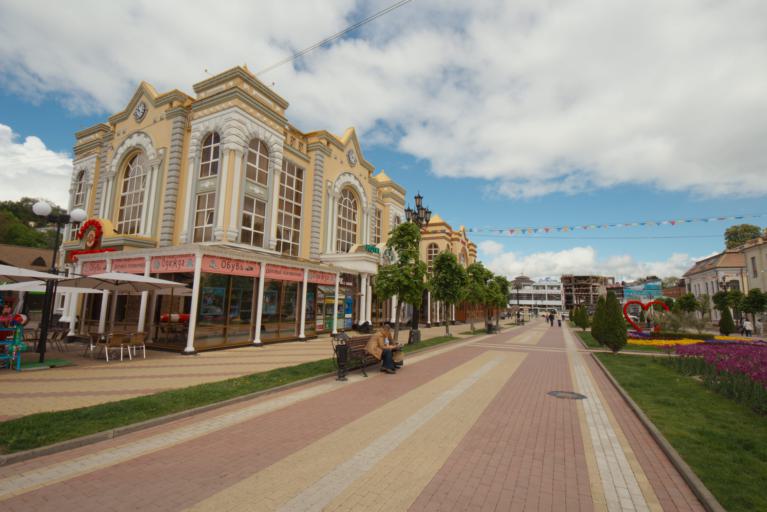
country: RU
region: Stavropol'skiy
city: Kislovodsk
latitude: 43.9041
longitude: 42.7167
